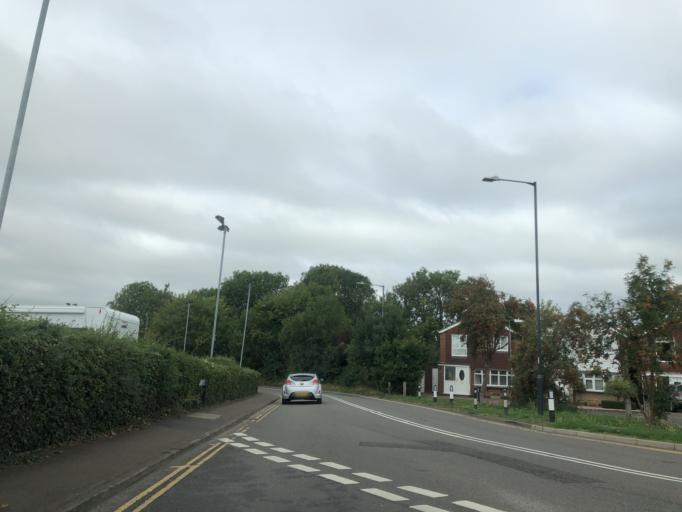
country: GB
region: England
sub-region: Warwickshire
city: Warwick
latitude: 52.2908
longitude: -1.5833
